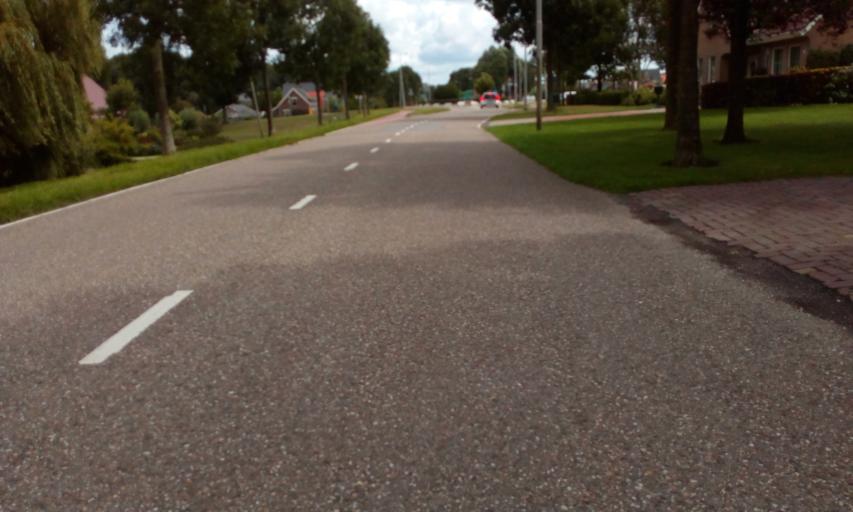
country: NL
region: South Holland
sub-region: Gemeente Barendrecht
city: Barendrecht
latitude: 51.8482
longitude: 4.5185
